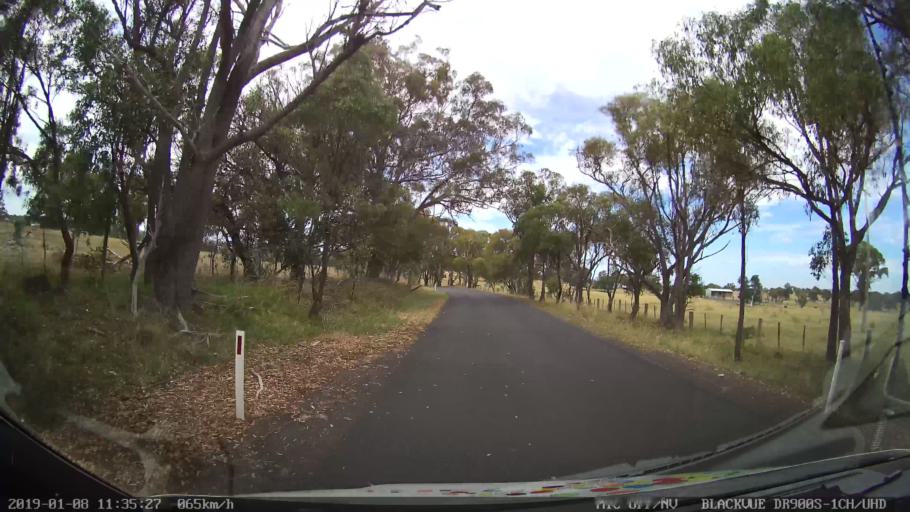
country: AU
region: New South Wales
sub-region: Guyra
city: Guyra
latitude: -30.3373
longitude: 151.5378
